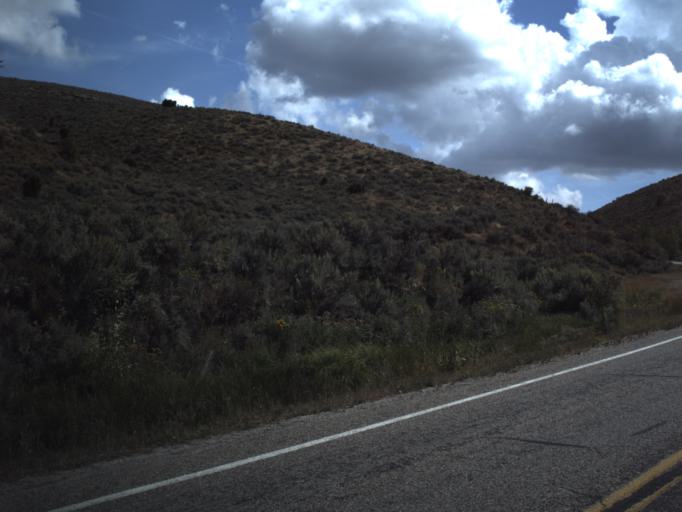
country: US
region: Utah
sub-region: Rich County
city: Randolph
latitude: 41.8211
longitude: -111.2897
